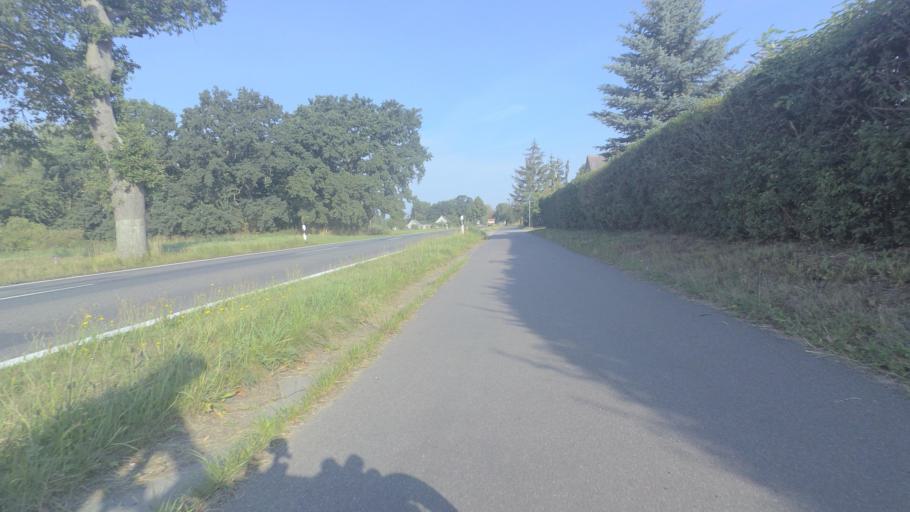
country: DE
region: Mecklenburg-Vorpommern
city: Grimmen
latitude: 54.0831
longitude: 13.1005
